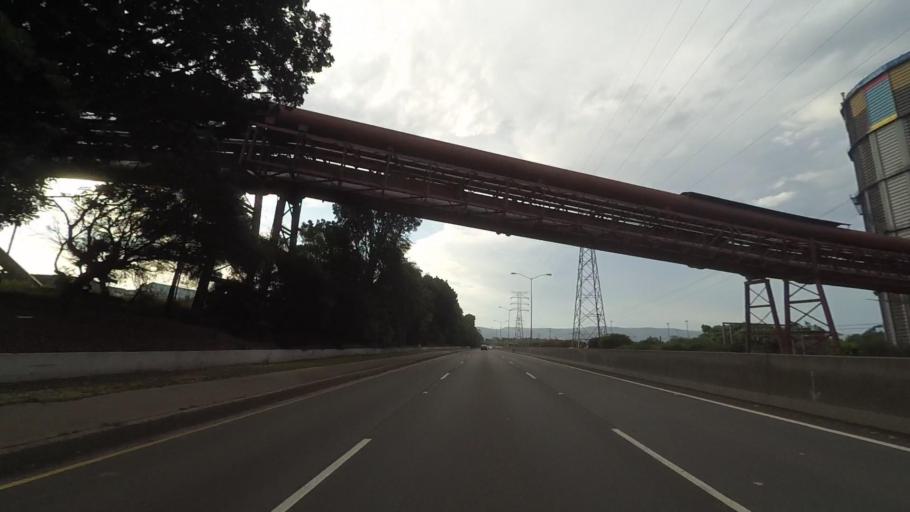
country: AU
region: New South Wales
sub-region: Wollongong
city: Cringila
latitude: -34.4704
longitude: 150.8818
